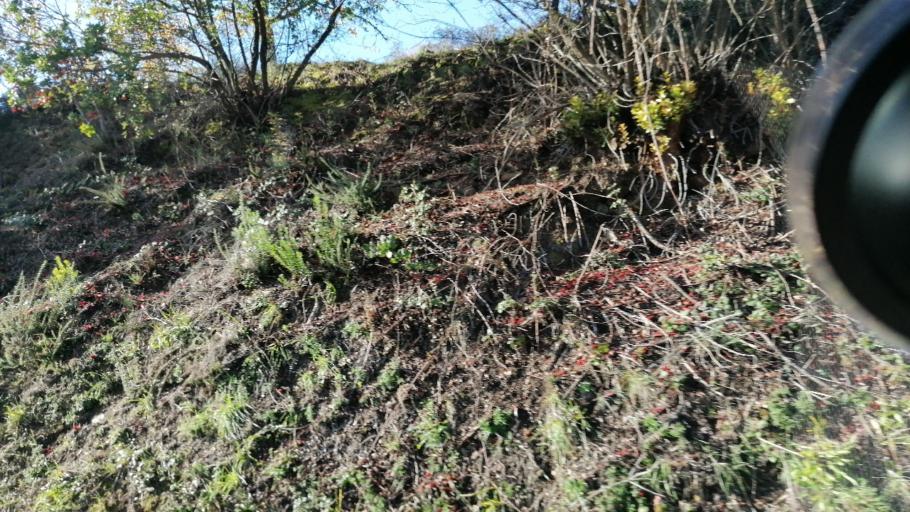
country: PT
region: Viseu
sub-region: Lamego
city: Lamego
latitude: 41.1084
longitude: -7.7907
